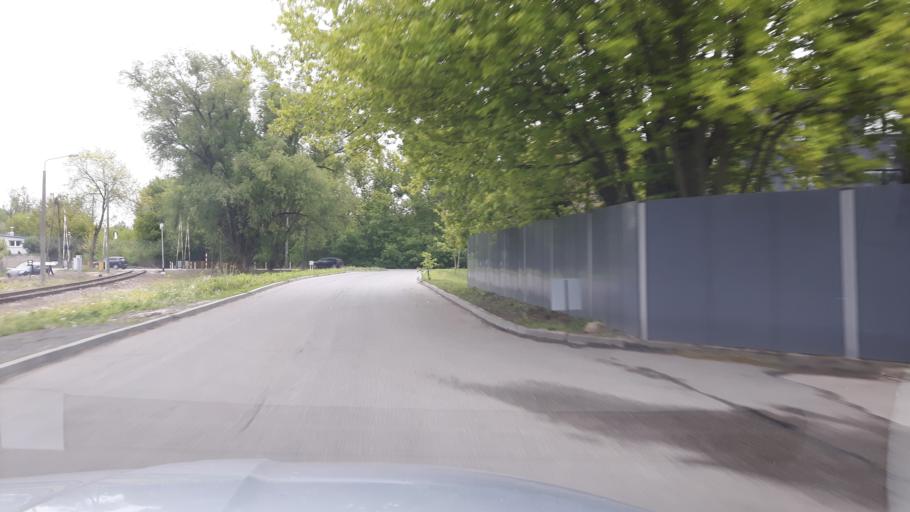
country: PL
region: Masovian Voivodeship
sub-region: Warszawa
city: Rembertow
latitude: 52.2602
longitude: 21.1354
